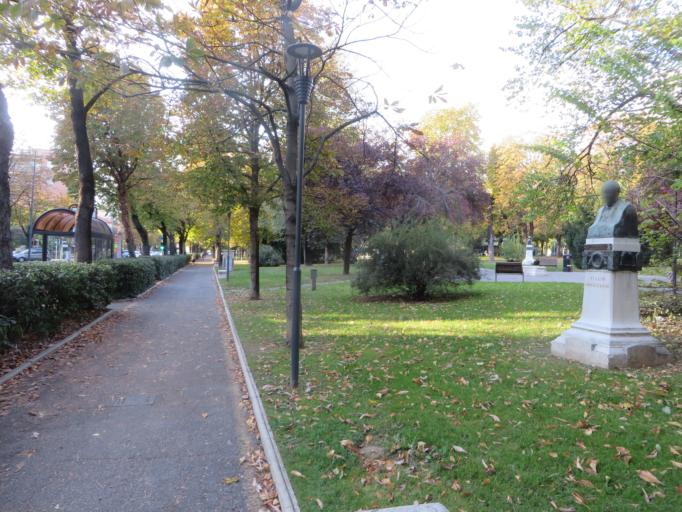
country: IT
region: Lombardy
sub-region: Provincia di Brescia
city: Brescia
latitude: 45.5344
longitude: 10.2383
